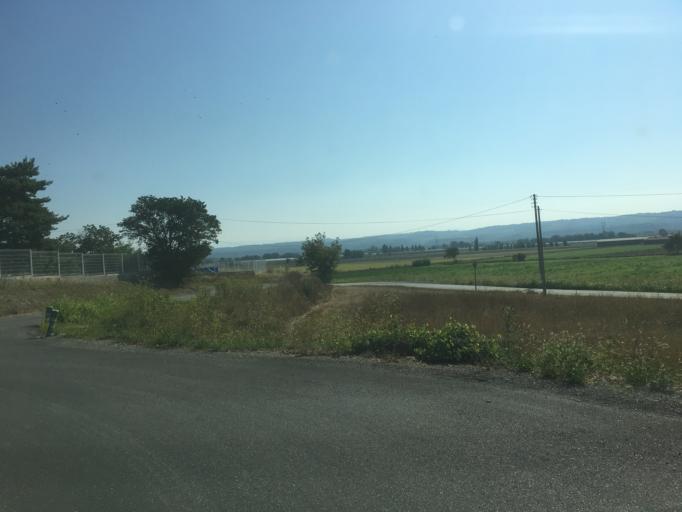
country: FR
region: Provence-Alpes-Cote d'Azur
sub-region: Departement des Alpes-de-Haute-Provence
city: Sainte-Tulle
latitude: 43.8004
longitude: 5.7862
